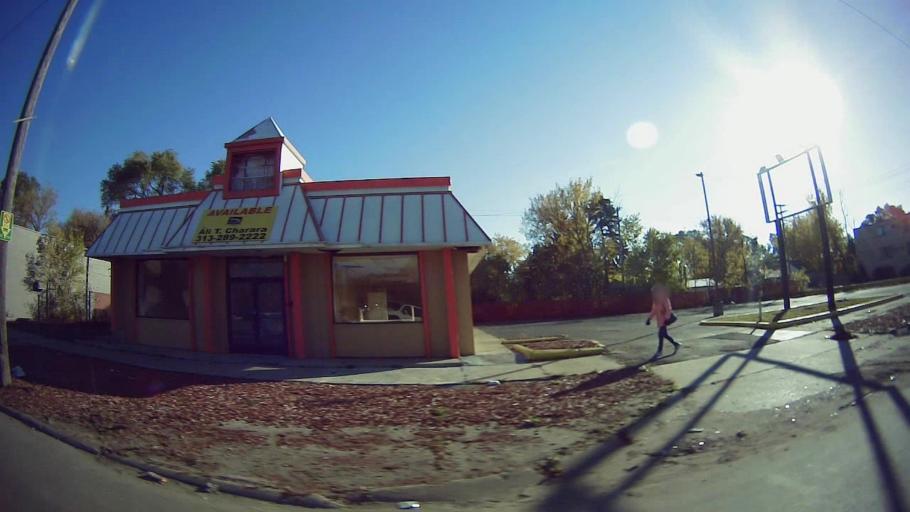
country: US
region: Michigan
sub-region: Wayne County
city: Dearborn
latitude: 42.3751
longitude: -83.1975
